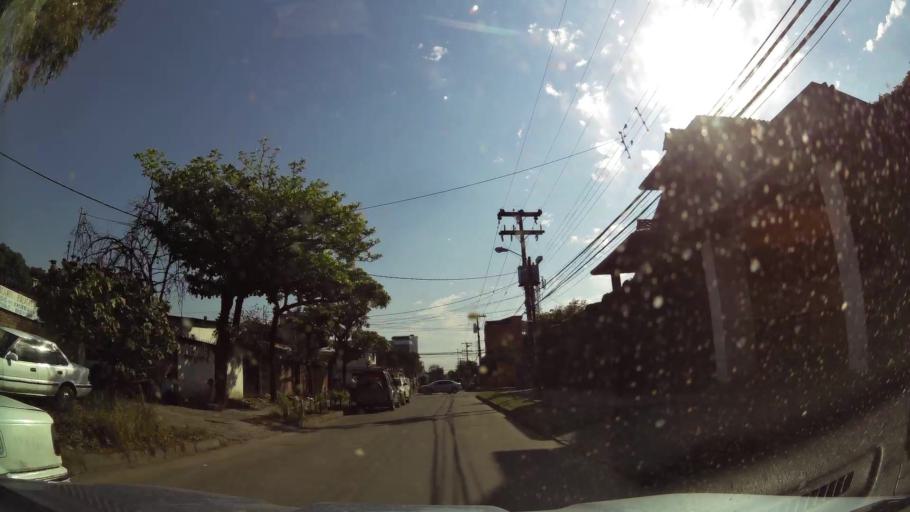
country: BO
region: Santa Cruz
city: Santa Cruz de la Sierra
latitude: -17.7833
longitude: -63.1637
